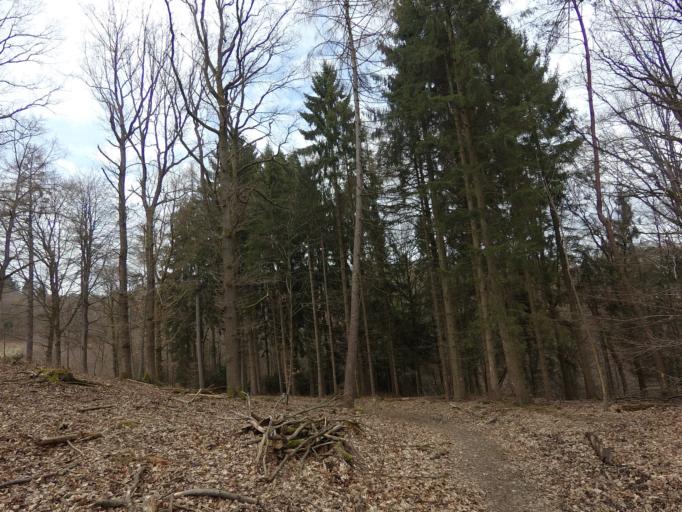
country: BE
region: Wallonia
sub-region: Province de Liege
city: Stoumont
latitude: 50.4102
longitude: 5.7279
